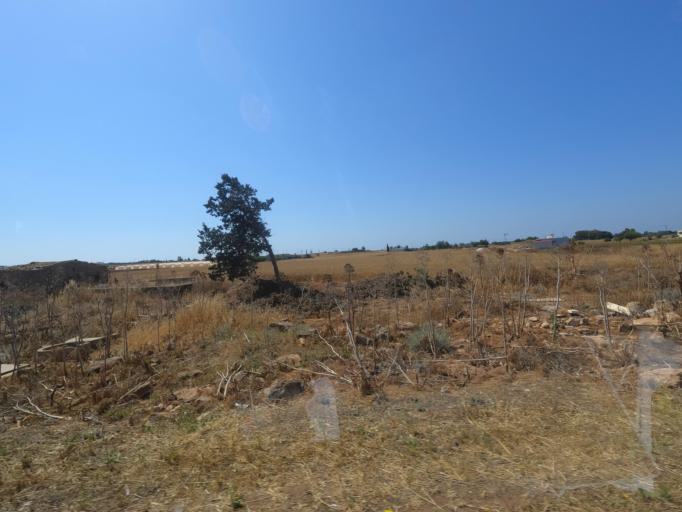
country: CY
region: Ammochostos
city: Frenaros
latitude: 35.0187
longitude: 33.9144
